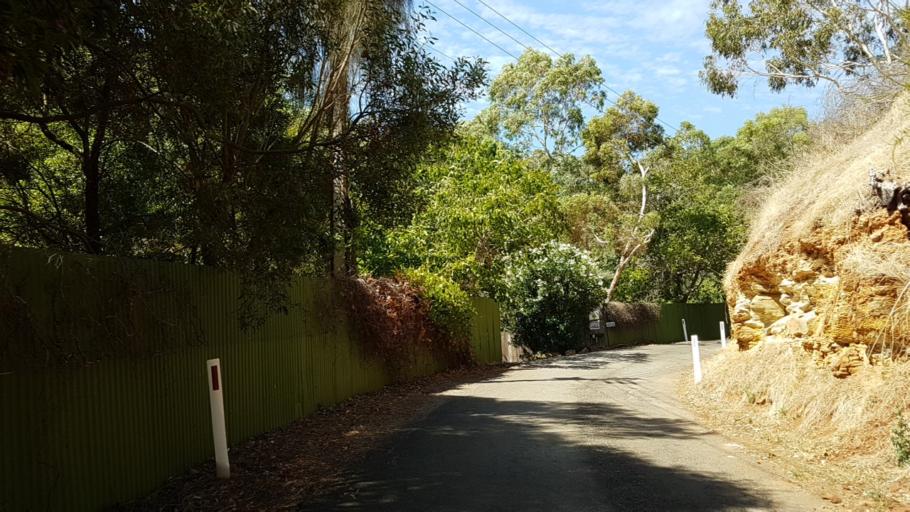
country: AU
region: South Australia
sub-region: Burnside
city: Mount Osmond
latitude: -34.9887
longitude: 138.6510
